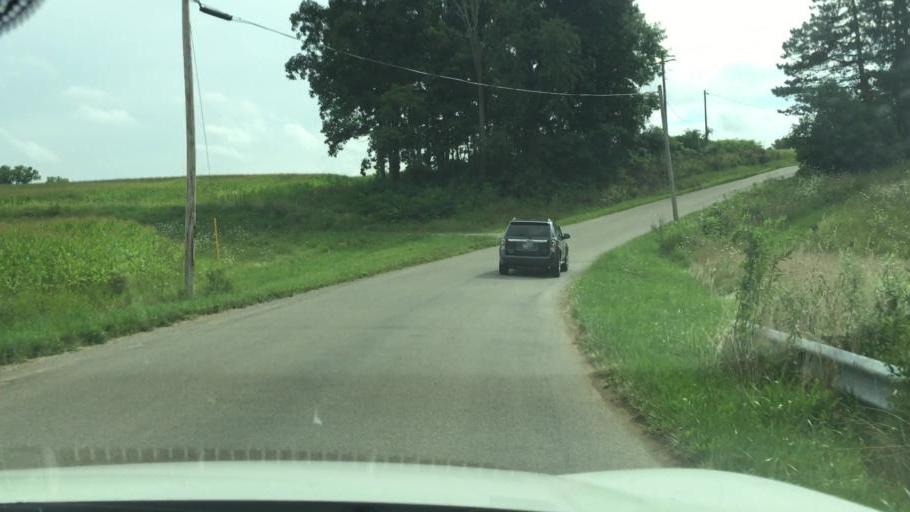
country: US
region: Ohio
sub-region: Champaign County
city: Mechanicsburg
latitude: 40.0313
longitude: -83.6053
